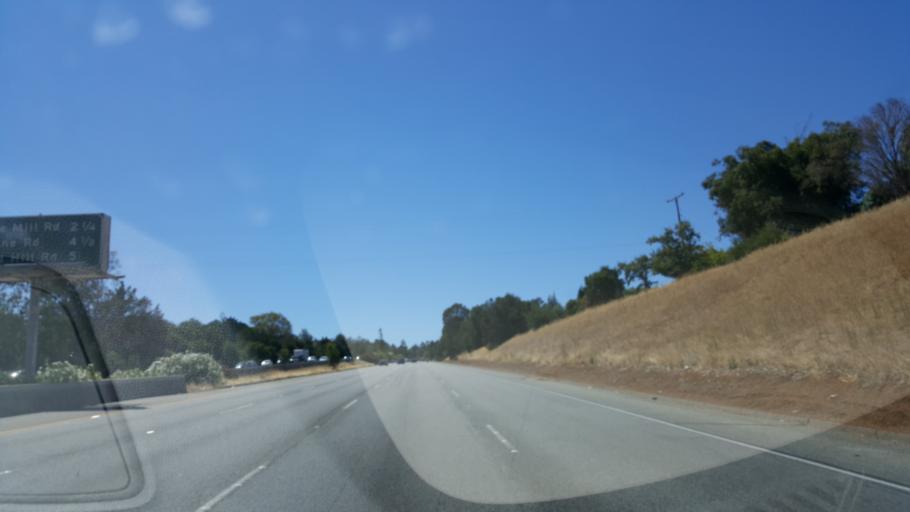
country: US
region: California
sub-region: Santa Clara County
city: Los Altos Hills
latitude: 37.3654
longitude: -122.1315
